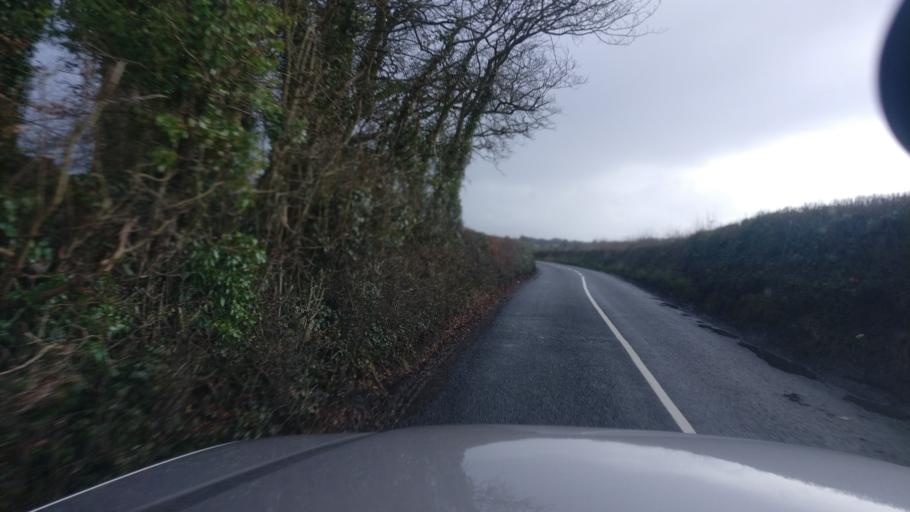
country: IE
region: Munster
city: Nenagh Bridge
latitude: 52.9664
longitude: -8.0877
